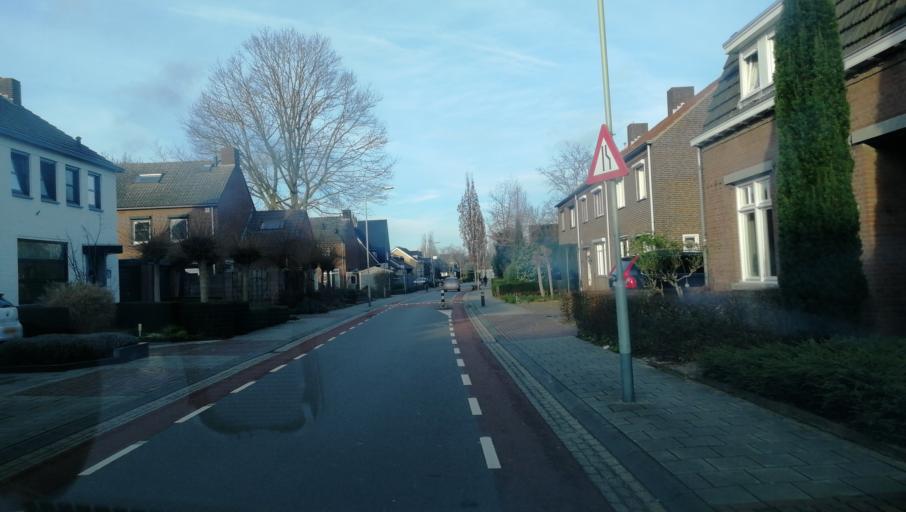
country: NL
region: Limburg
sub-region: Gemeente Venlo
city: Tegelen
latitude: 51.3346
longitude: 6.0980
